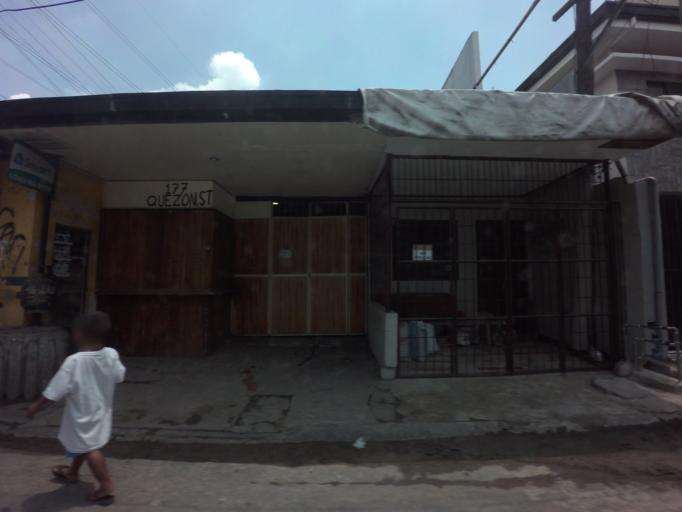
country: PH
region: Calabarzon
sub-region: Province of Laguna
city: San Pedro
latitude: 14.3907
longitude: 121.0480
